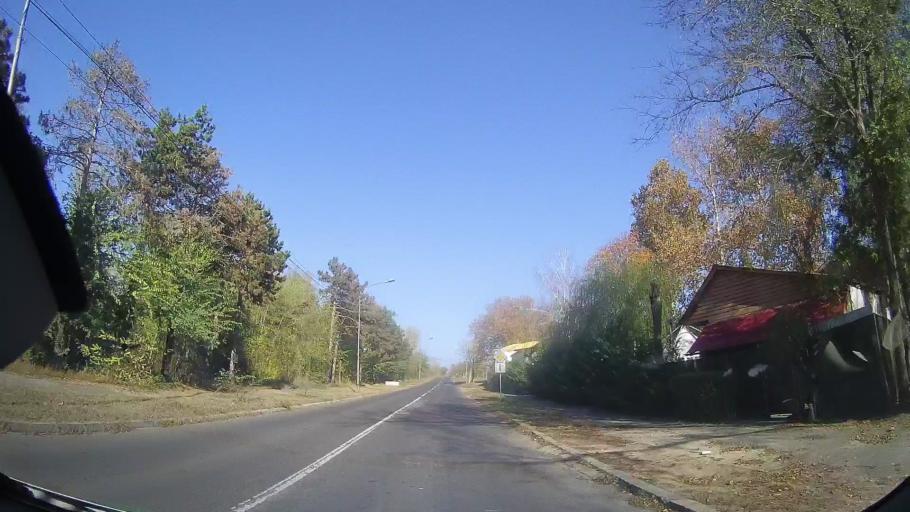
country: RO
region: Constanta
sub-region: Municipiul Mangalia
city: Mangalia
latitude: 43.8465
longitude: 28.5894
